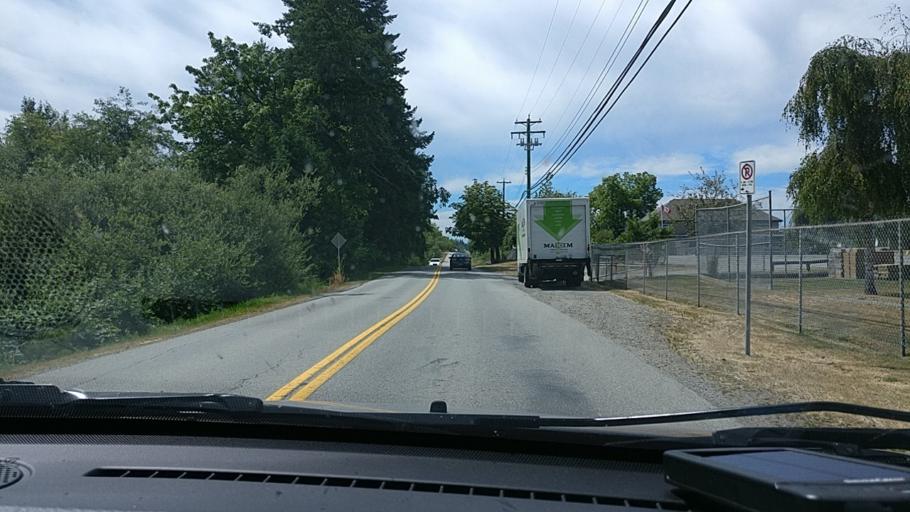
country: US
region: Washington
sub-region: Whatcom County
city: Blaine
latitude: 49.0167
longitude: -122.7216
